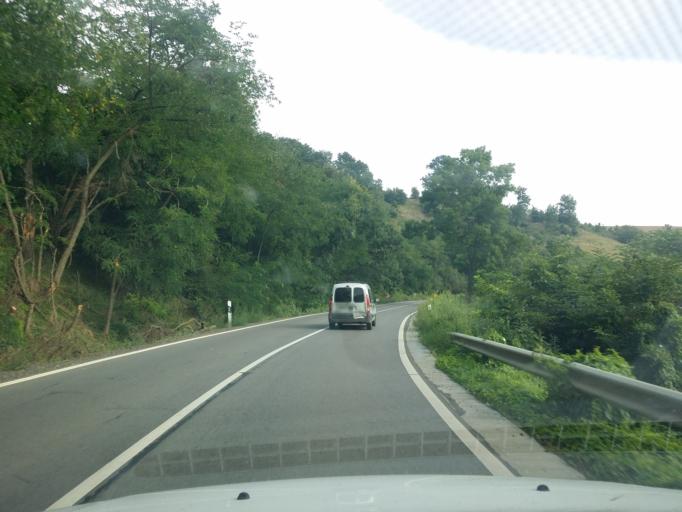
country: HU
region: Pest
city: Acsa
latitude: 47.7905
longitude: 19.3648
